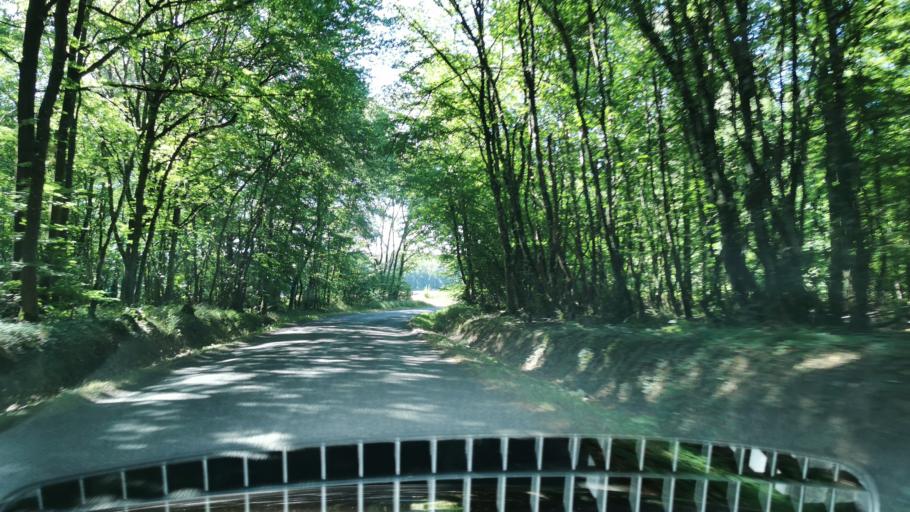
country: FR
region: Bourgogne
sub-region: Departement de Saone-et-Loire
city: Torcy
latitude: 46.7694
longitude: 4.4724
